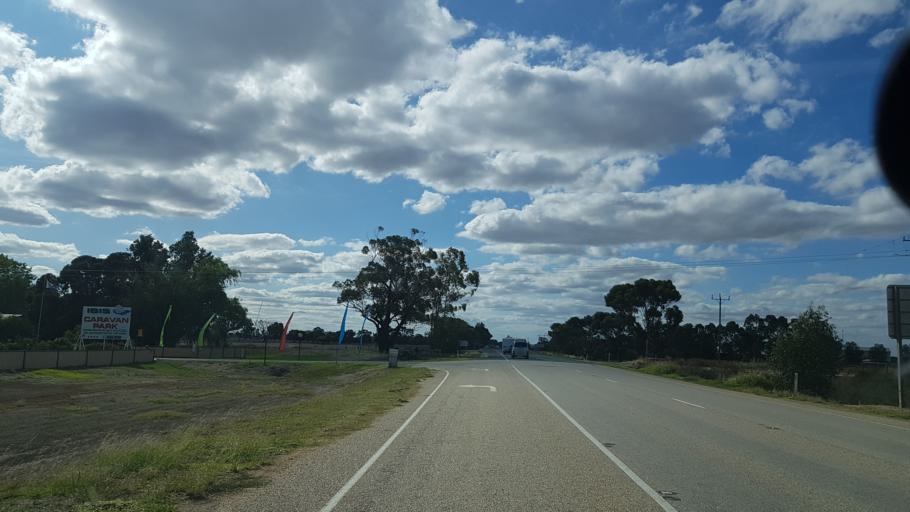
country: AU
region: Victoria
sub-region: Swan Hill
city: Swan Hill
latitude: -35.7606
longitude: 143.9299
